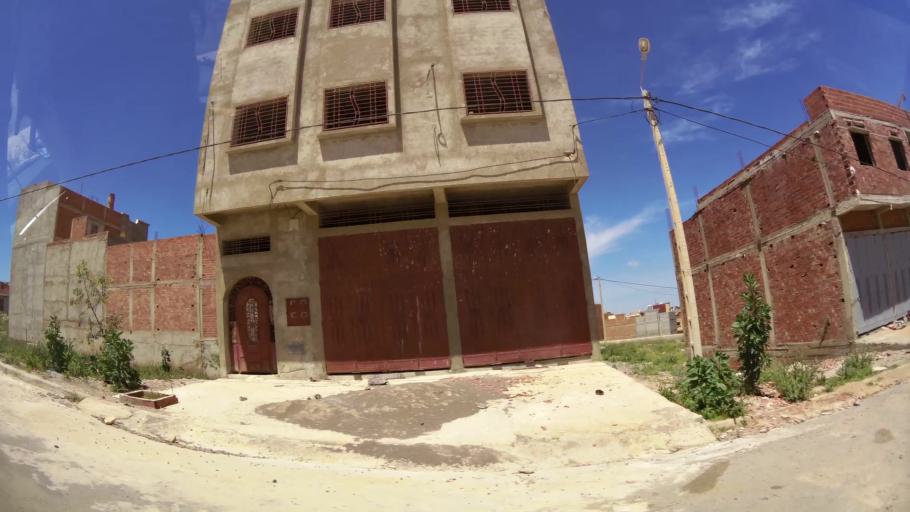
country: MA
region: Oriental
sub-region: Oujda-Angad
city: Oujda
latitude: 34.6539
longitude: -1.9469
